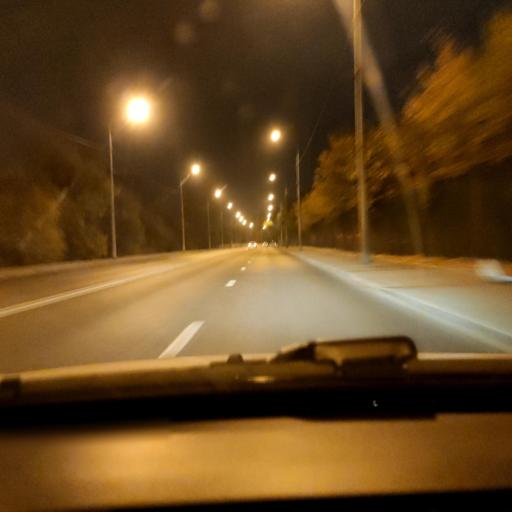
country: RU
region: Voronezj
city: Voronezh
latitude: 51.6902
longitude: 39.2321
